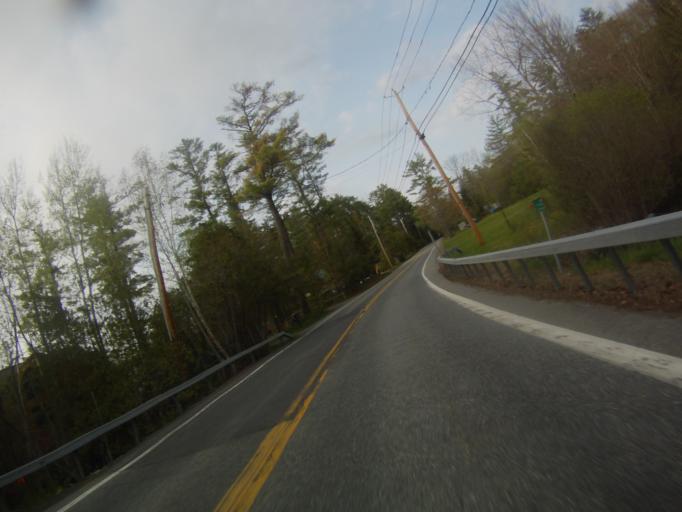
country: US
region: New York
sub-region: Warren County
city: Warrensburg
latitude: 43.7299
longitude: -73.6757
